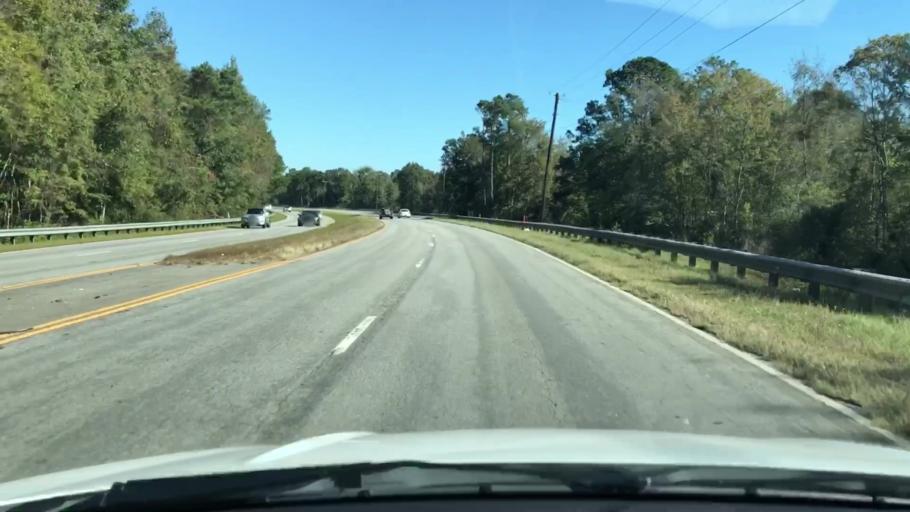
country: US
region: South Carolina
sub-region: Charleston County
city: Ravenel
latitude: 32.7629
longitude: -80.4411
